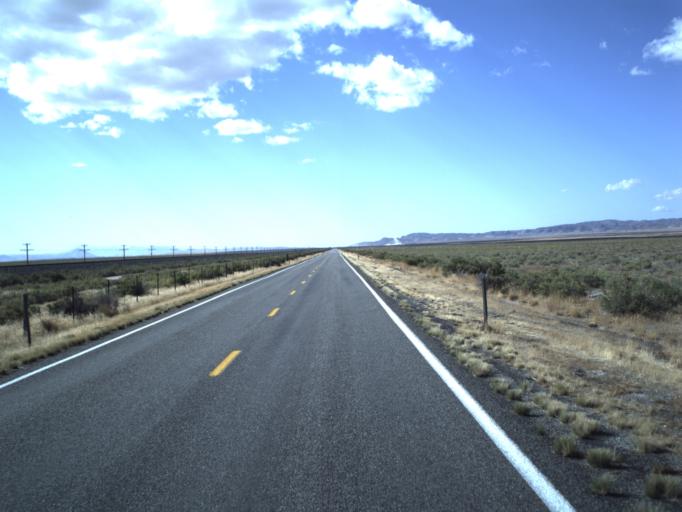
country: US
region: Utah
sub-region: Millard County
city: Delta
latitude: 39.0681
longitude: -112.7604
